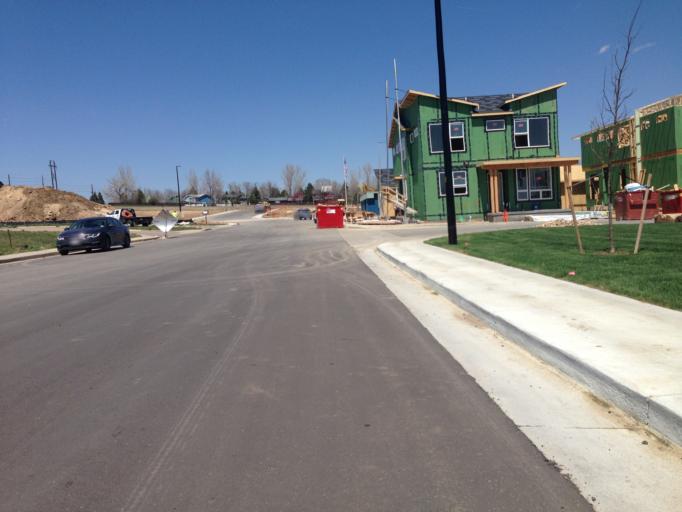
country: US
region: Colorado
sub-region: Boulder County
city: Louisville
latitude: 39.9881
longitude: -105.1173
